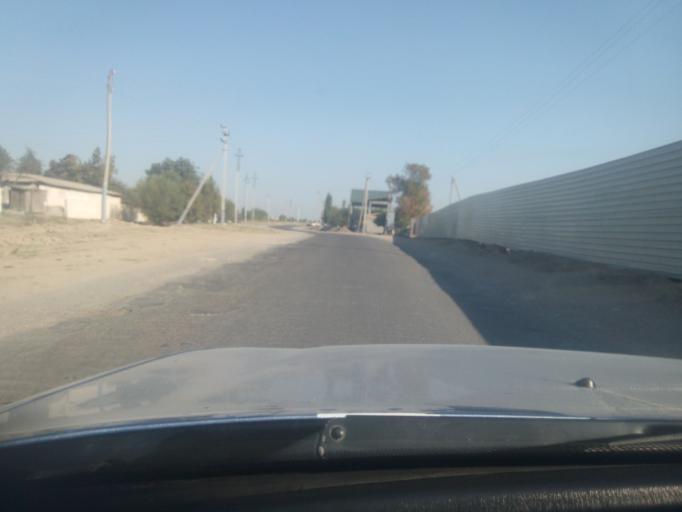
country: UZ
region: Sirdaryo
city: Guliston
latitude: 40.4953
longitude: 68.8004
